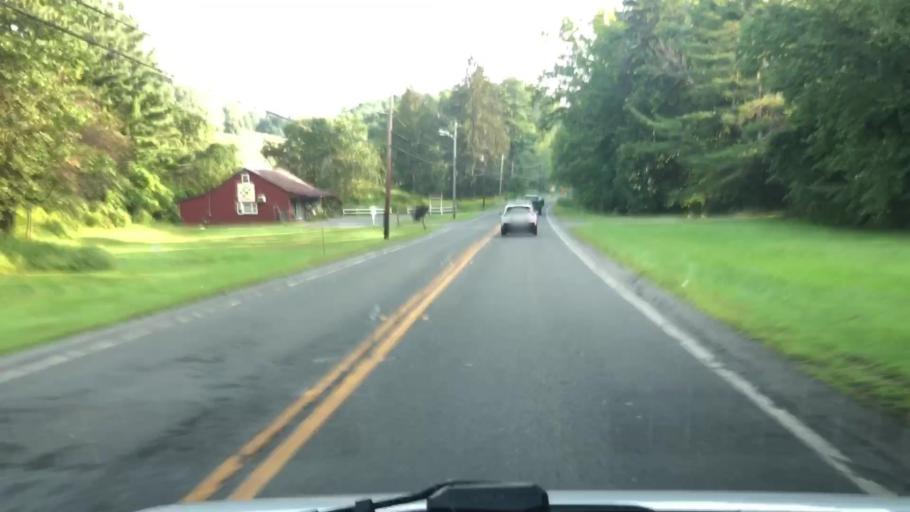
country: US
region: Massachusetts
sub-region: Berkshire County
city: Williamstown
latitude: 42.6979
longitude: -73.2253
